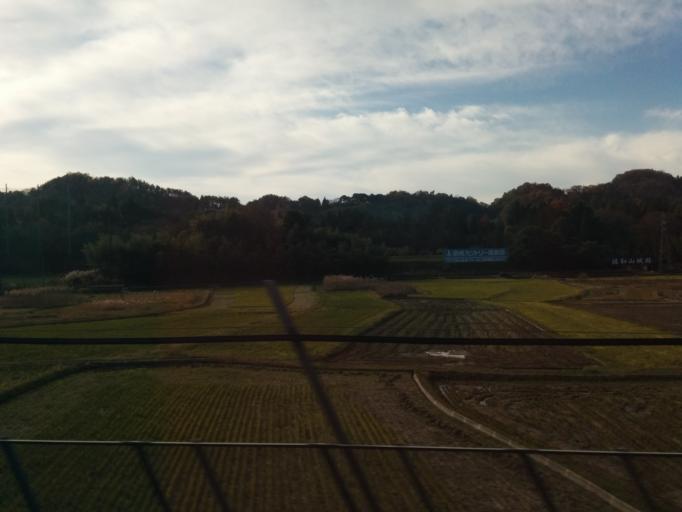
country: JP
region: Shiga Prefecture
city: Hikone
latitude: 35.2757
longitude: 136.2802
